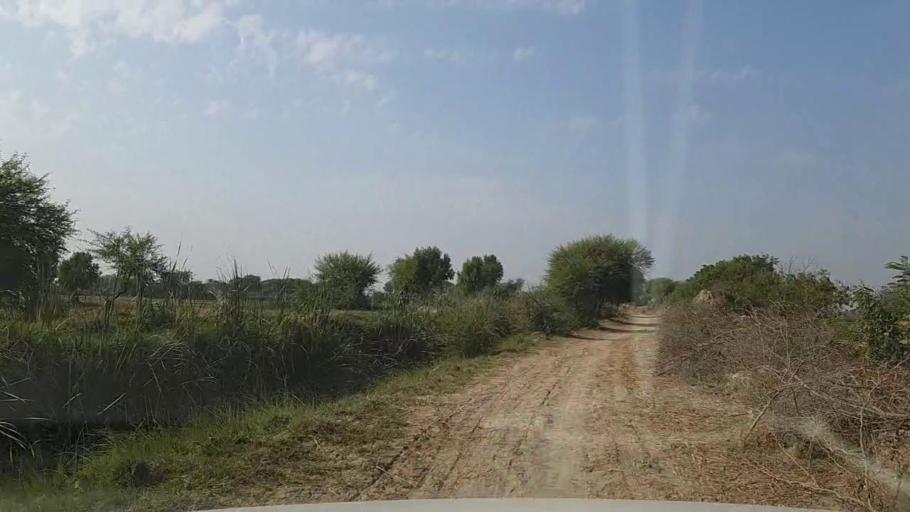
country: PK
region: Sindh
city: Mirpur Batoro
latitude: 24.7101
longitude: 68.2981
